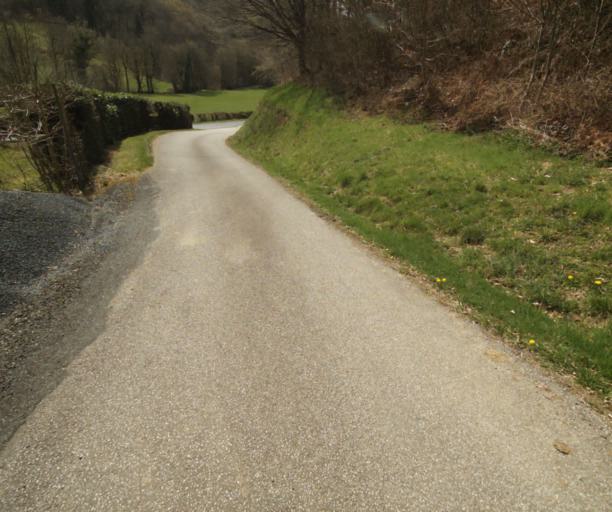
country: FR
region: Limousin
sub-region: Departement de la Correze
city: Naves
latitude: 45.3411
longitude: 1.7999
